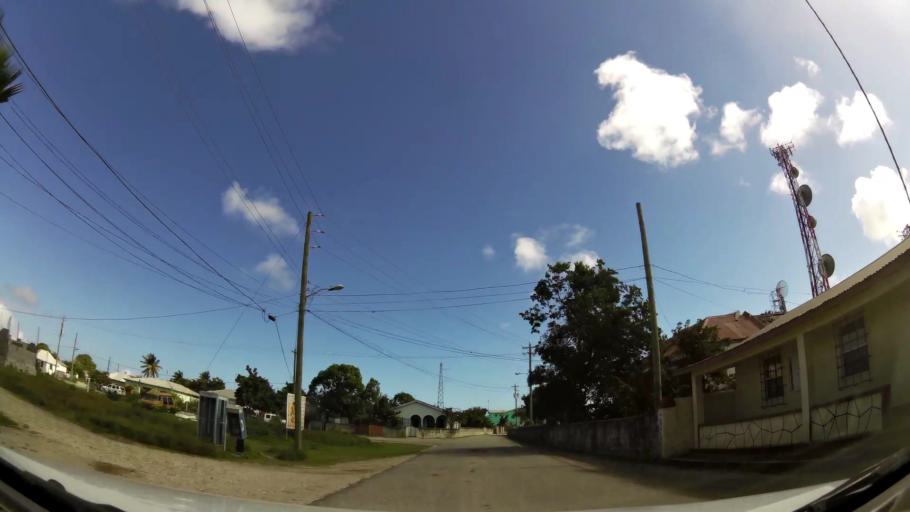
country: AG
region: Barbuda
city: Codrington
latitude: 17.6413
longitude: -61.8260
